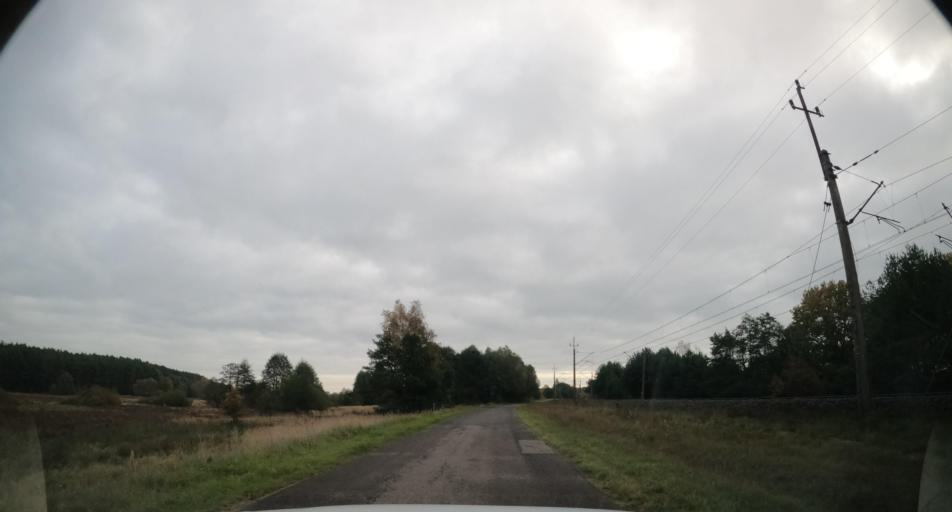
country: PL
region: West Pomeranian Voivodeship
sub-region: Powiat kamienski
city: Miedzyzdroje
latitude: 53.9260
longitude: 14.5492
